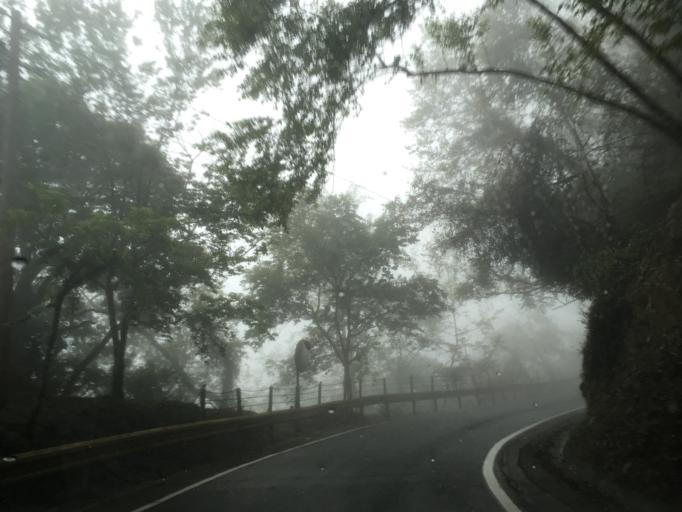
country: TW
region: Taiwan
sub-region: Hualien
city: Hualian
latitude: 24.1910
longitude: 121.4199
